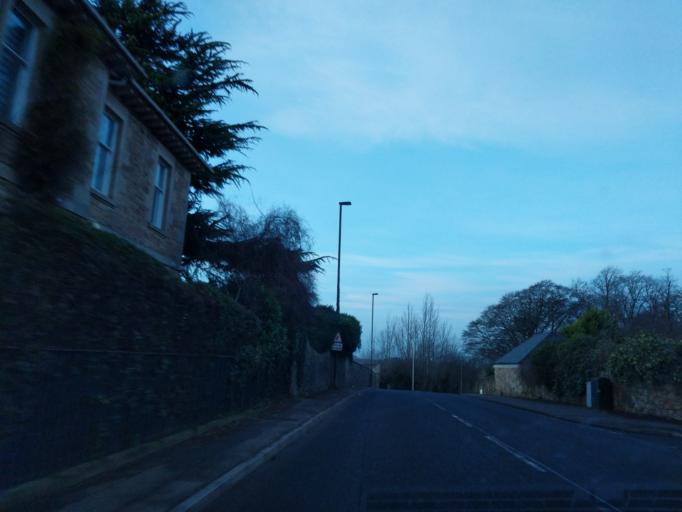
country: GB
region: Scotland
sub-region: Midlothian
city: Bonnyrigg
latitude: 55.8813
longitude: -3.1112
